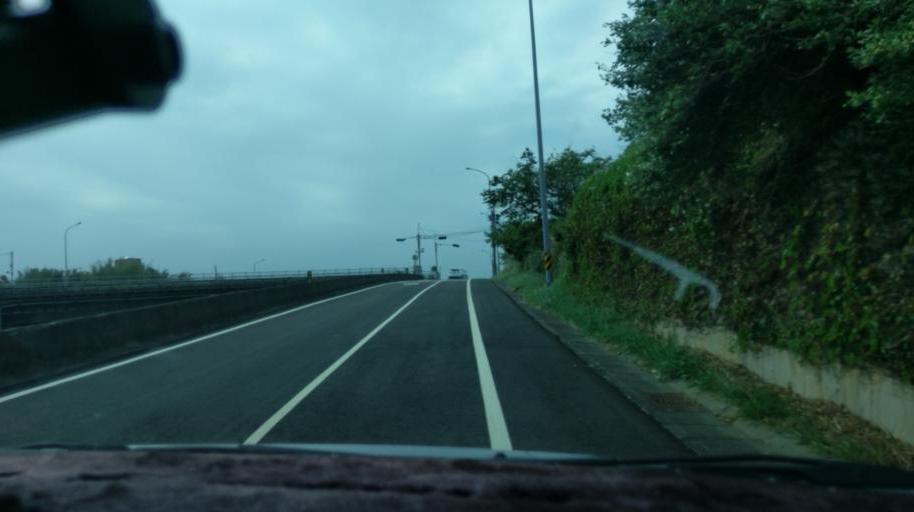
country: TW
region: Taiwan
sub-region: Miaoli
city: Miaoli
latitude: 24.5884
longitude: 120.7311
